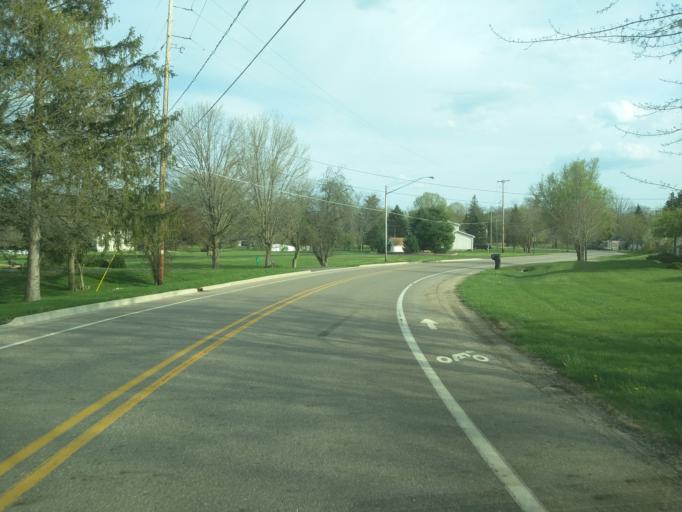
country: US
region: Michigan
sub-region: Eaton County
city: Dimondale
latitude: 42.6422
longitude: -84.6493
